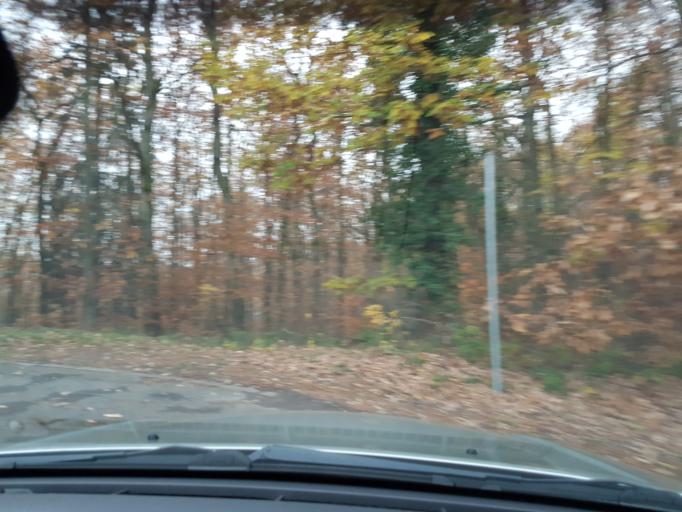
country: DE
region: Hesse
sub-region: Regierungsbezirk Darmstadt
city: Kiedrich
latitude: 50.0404
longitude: 8.0582
